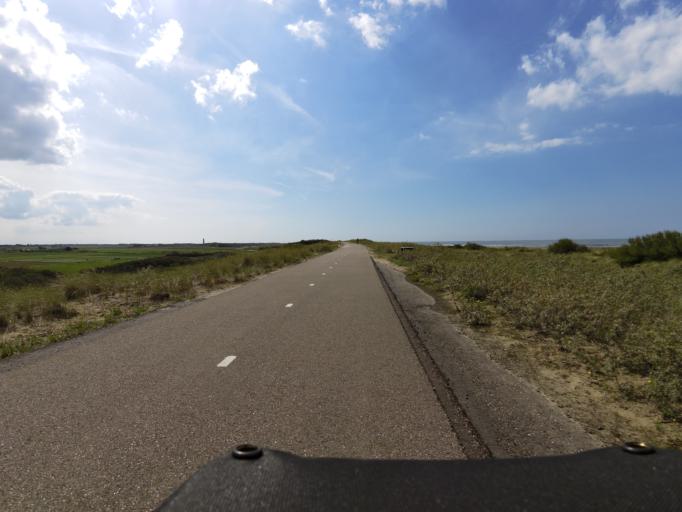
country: NL
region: South Holland
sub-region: Gemeente Goeree-Overflakkee
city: Ouddorp
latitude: 51.8247
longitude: 3.9037
